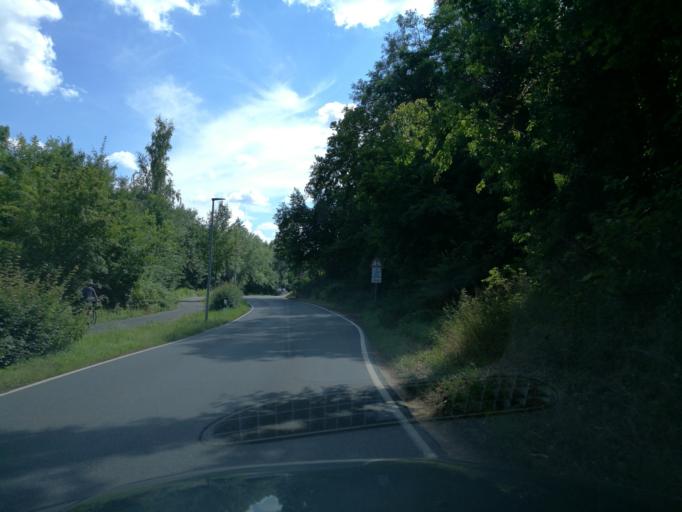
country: DE
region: Bavaria
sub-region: Regierungsbezirk Mittelfranken
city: Furth
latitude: 49.4947
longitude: 10.9666
